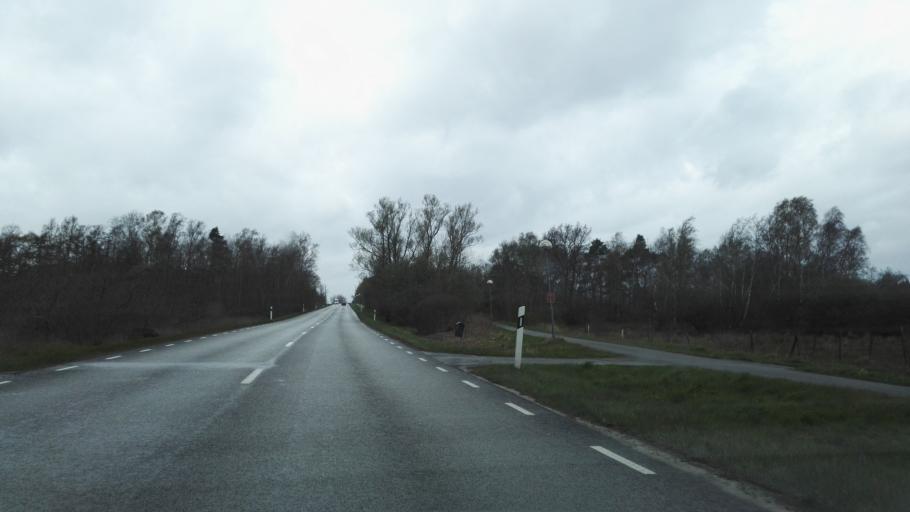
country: SE
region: Skane
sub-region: Simrishamns Kommun
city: Simrishamn
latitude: 55.5823
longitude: 14.3276
